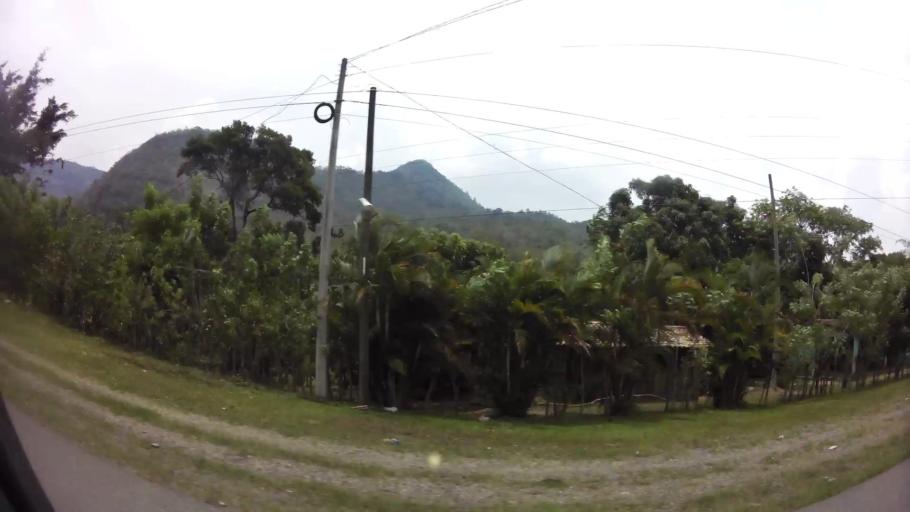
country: HN
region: Comayagua
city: Taulabe
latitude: 14.7242
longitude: -87.9648
